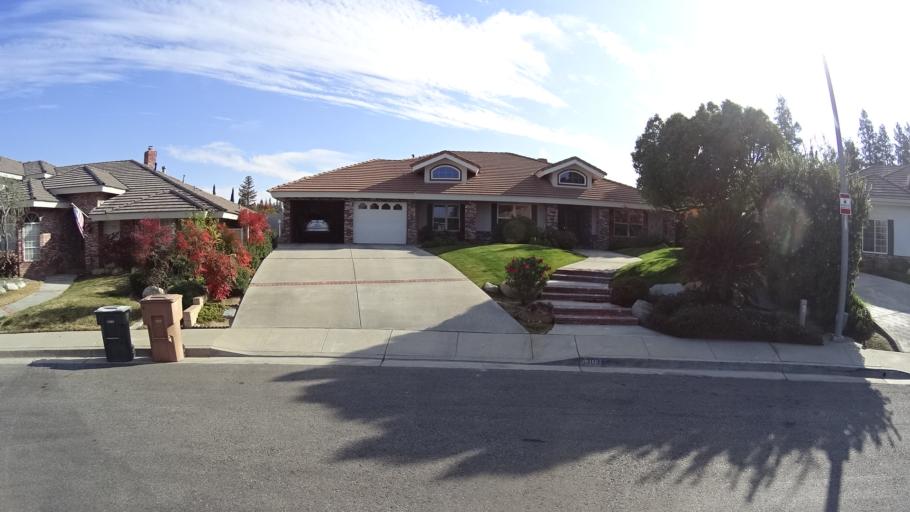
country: US
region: California
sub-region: Kern County
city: Oildale
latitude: 35.4022
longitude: -118.9171
